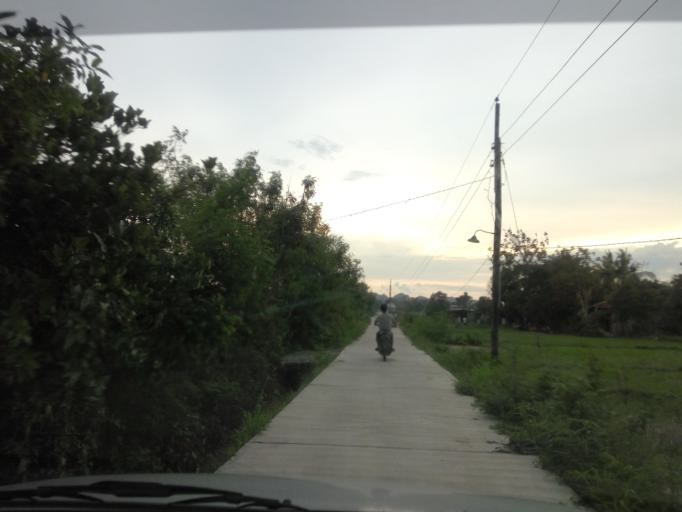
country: PH
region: Ilocos
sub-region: Province of La Union
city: Subusub
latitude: 16.2087
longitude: 120.4836
